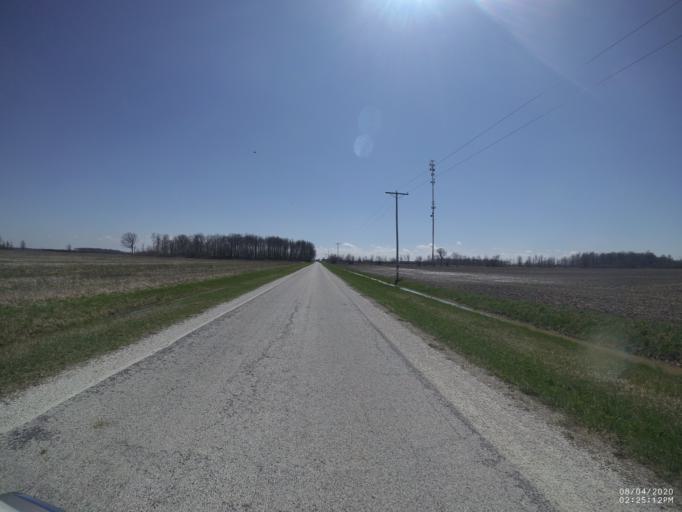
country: US
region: Ohio
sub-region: Sandusky County
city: Gibsonburg
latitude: 41.3004
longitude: -83.2595
